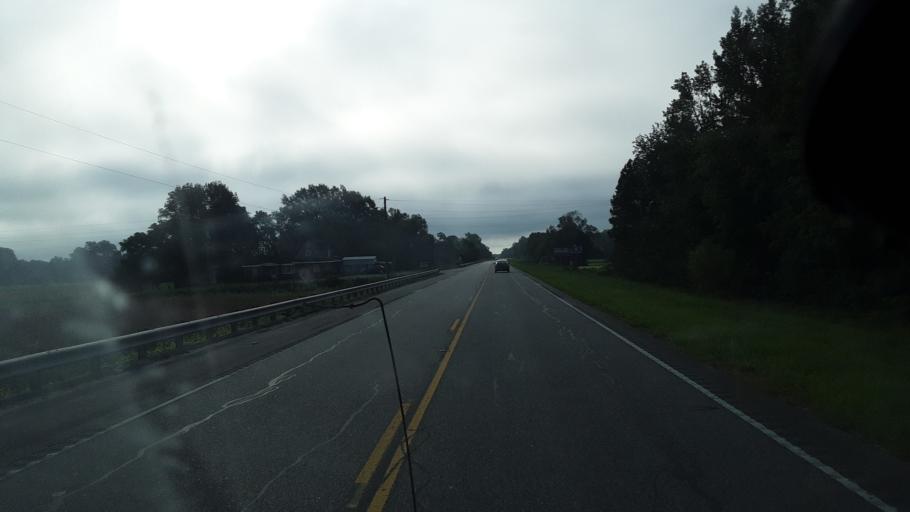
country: US
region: South Carolina
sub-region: Horry County
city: Red Hill
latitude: 33.8464
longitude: -79.2856
